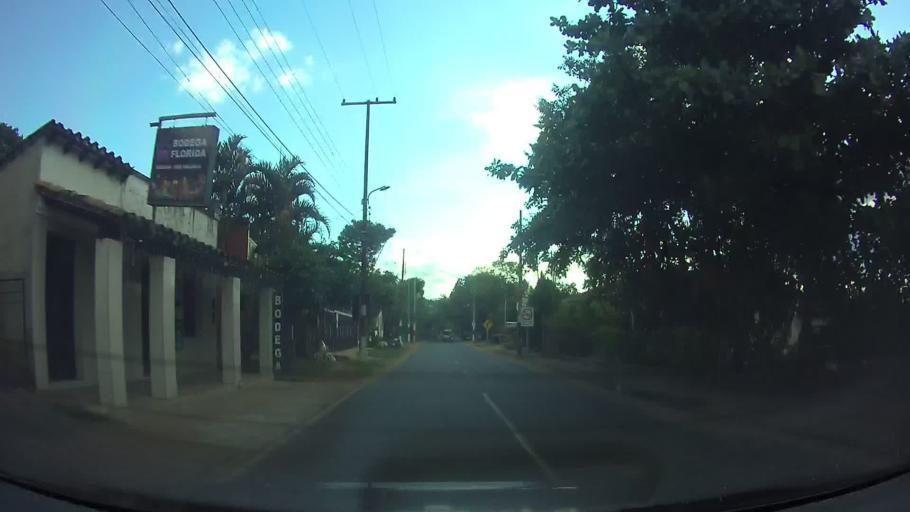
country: PY
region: Central
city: Aregua
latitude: -25.2785
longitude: -57.4319
